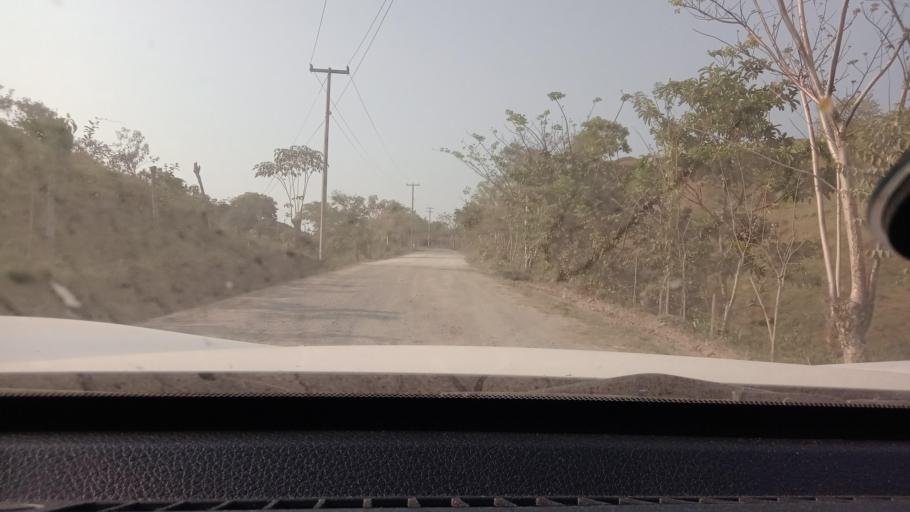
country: MX
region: Tabasco
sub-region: Huimanguillo
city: Francisco Rueda
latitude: 17.6620
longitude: -93.8623
